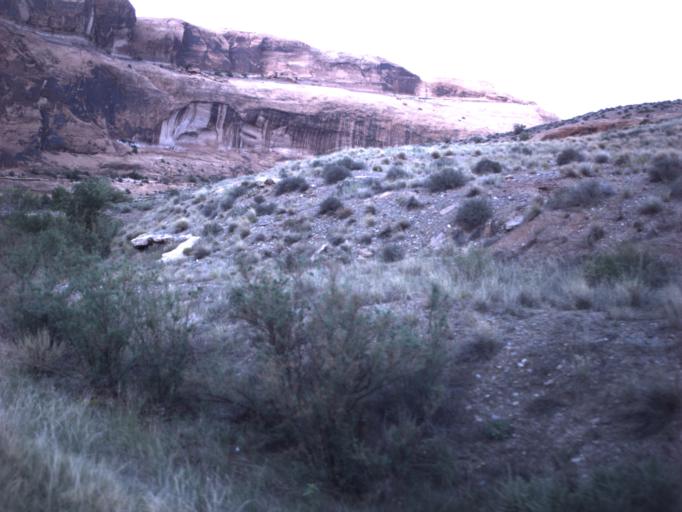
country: US
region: Utah
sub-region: Grand County
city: Moab
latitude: 38.6105
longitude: -109.5574
